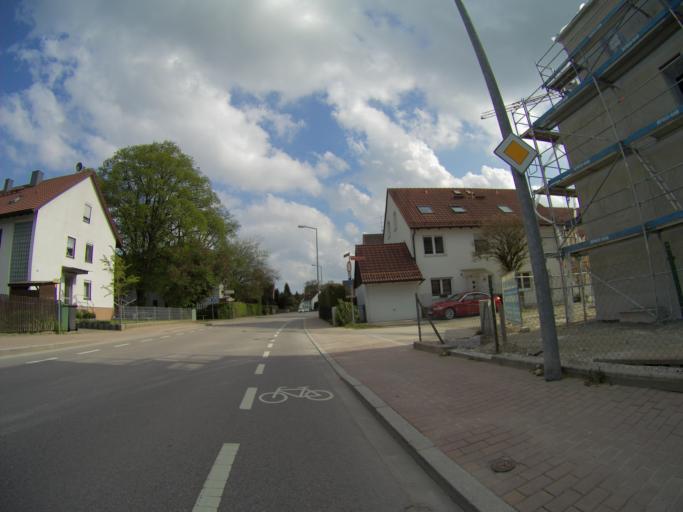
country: DE
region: Bavaria
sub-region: Upper Bavaria
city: Freising
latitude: 48.3940
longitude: 11.7528
